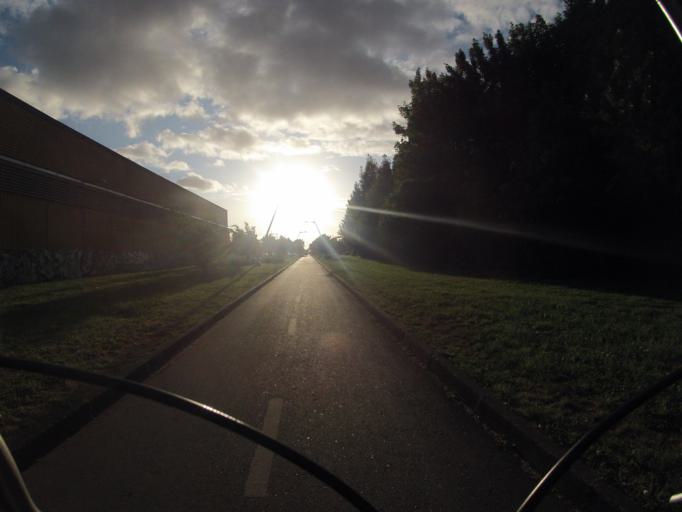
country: CL
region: Araucania
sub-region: Provincia de Cautin
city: Temuco
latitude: -38.7437
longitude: -72.6108
